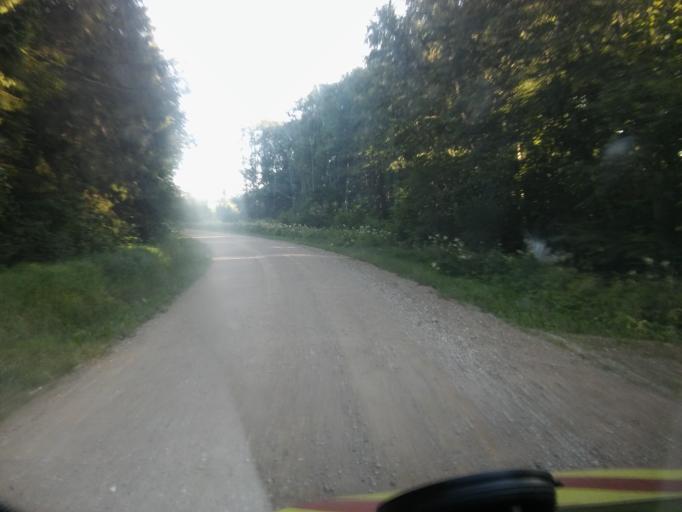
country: EE
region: Valgamaa
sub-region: Torva linn
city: Torva
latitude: 58.0738
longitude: 25.9021
